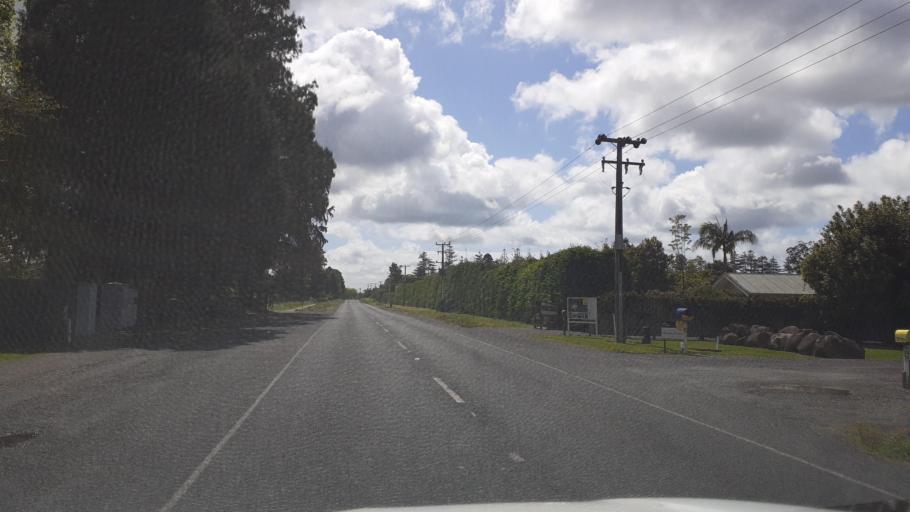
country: NZ
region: Northland
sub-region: Far North District
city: Kerikeri
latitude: -35.2251
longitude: 173.9715
